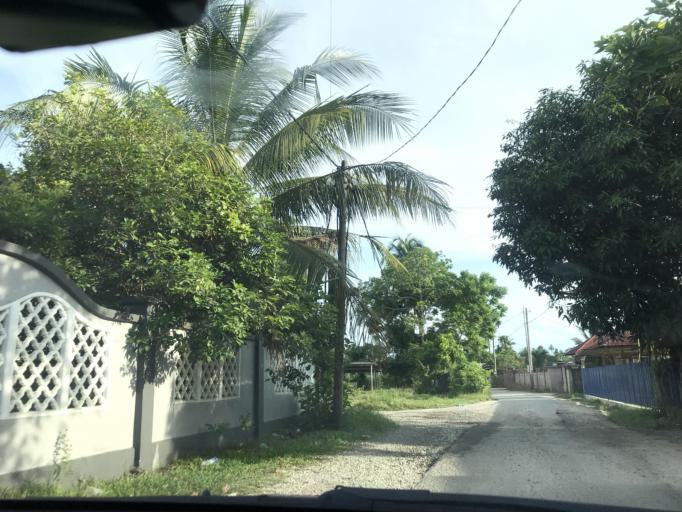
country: MY
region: Kelantan
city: Kota Bharu
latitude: 6.1325
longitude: 102.2227
